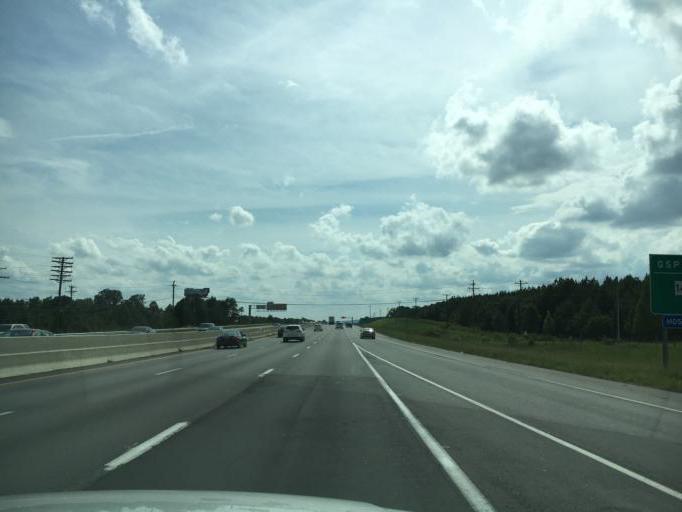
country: US
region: South Carolina
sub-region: Greenville County
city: Greer
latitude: 34.8841
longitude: -82.1972
